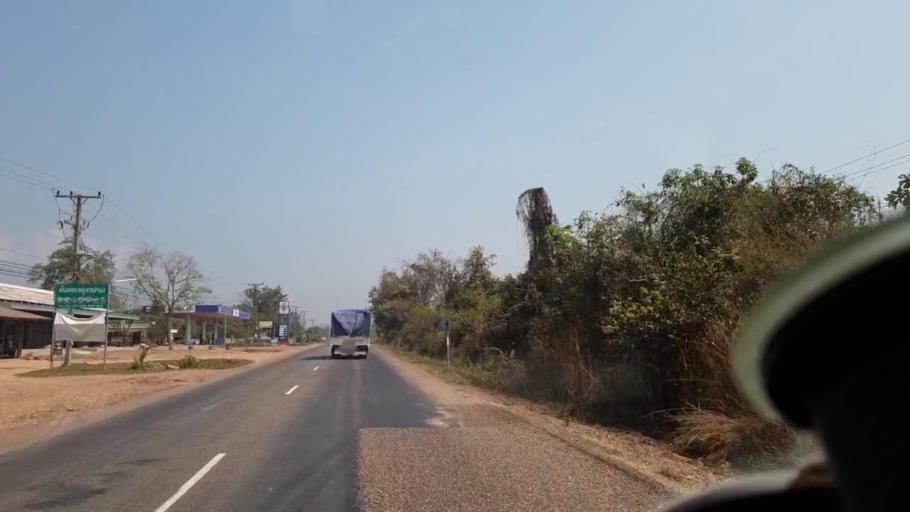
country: TH
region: Nong Khai
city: Phon Phisai
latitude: 18.0963
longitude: 103.0165
